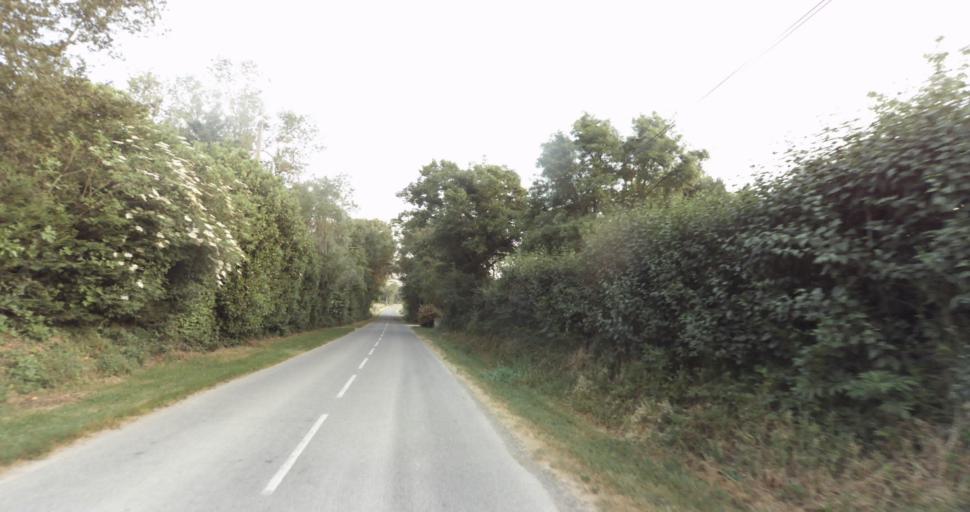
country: FR
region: Midi-Pyrenees
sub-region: Departement de la Haute-Garonne
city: Levignac
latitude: 43.6473
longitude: 1.1550
